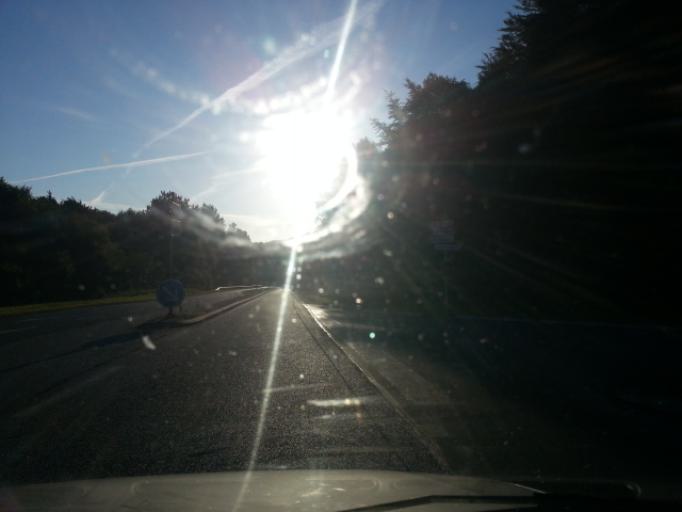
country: FR
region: Brittany
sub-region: Departement du Morbihan
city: Gourin
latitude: 48.1739
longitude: -3.5732
